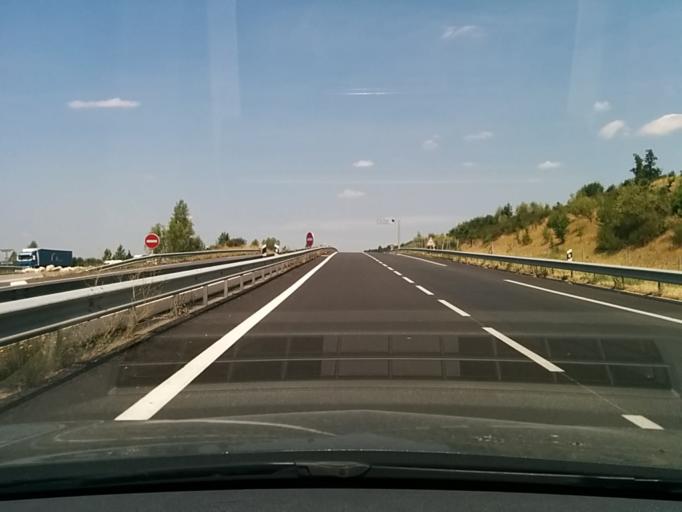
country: FR
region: Midi-Pyrenees
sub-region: Departement du Gers
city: Pujaudran
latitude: 43.5869
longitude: 1.1269
